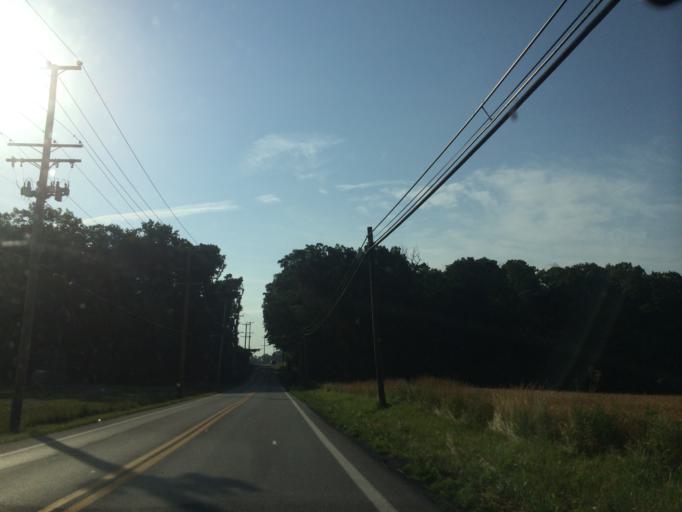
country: US
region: Maryland
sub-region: Carroll County
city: Sykesville
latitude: 39.3835
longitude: -77.0003
